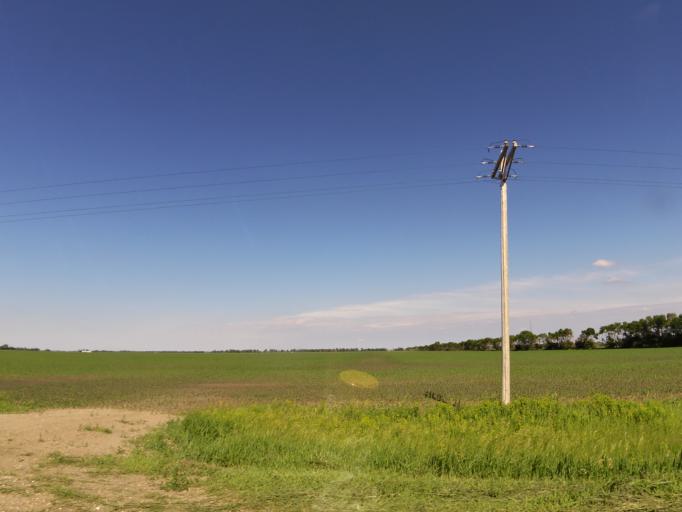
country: US
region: North Dakota
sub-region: Walsh County
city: Grafton
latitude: 48.3036
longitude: -97.2550
